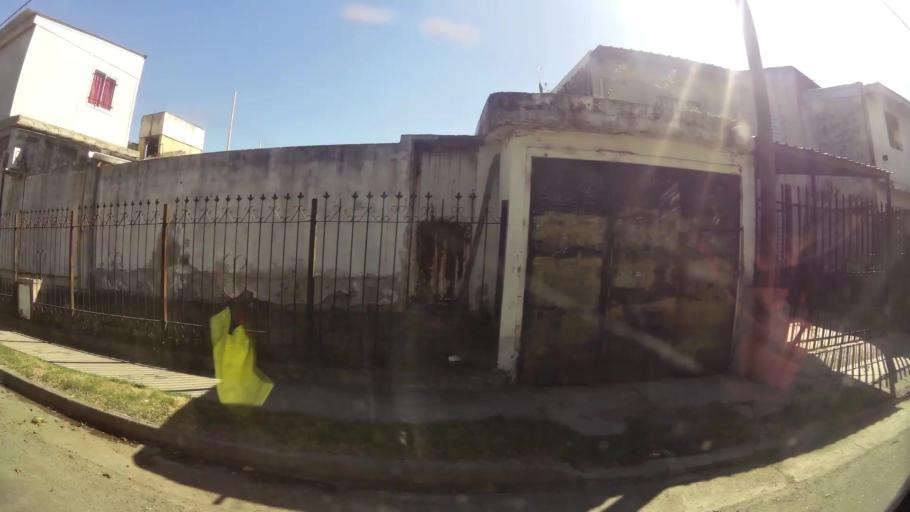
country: AR
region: Cordoba
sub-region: Departamento de Capital
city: Cordoba
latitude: -31.3668
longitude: -64.1629
